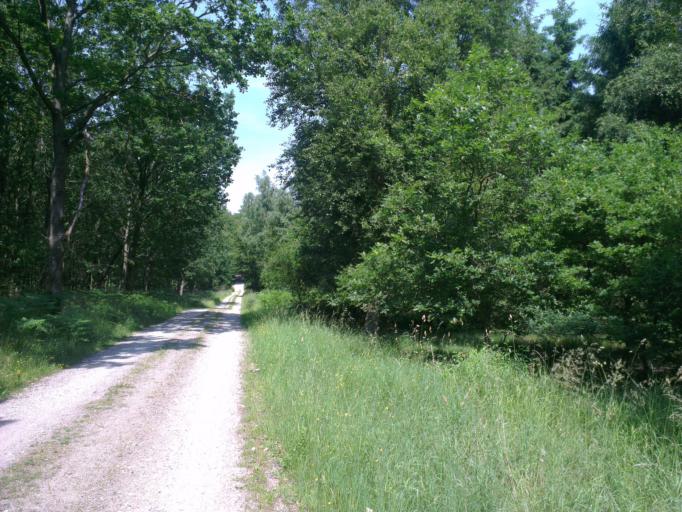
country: DK
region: Capital Region
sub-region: Allerod Kommune
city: Lillerod
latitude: 55.9176
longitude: 12.3519
